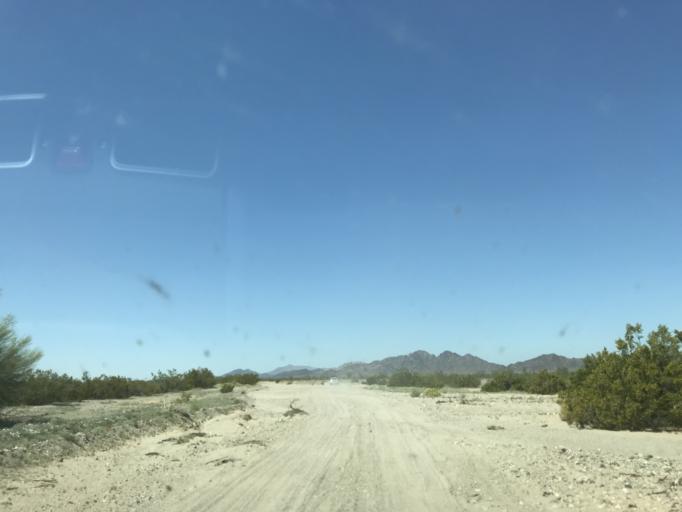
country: US
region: California
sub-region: Riverside County
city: Mesa Verde
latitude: 33.4893
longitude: -114.8943
